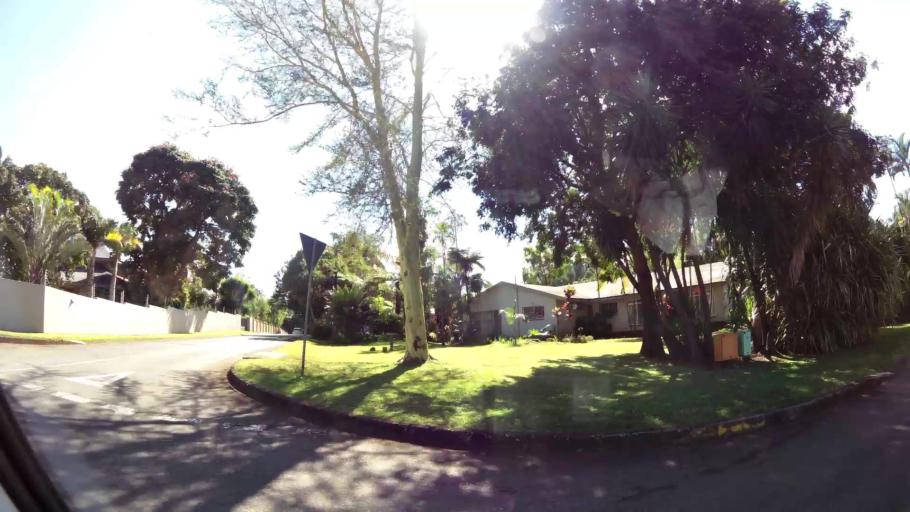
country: ZA
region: Limpopo
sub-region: Mopani District Municipality
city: Tzaneen
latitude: -23.8111
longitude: 30.1531
